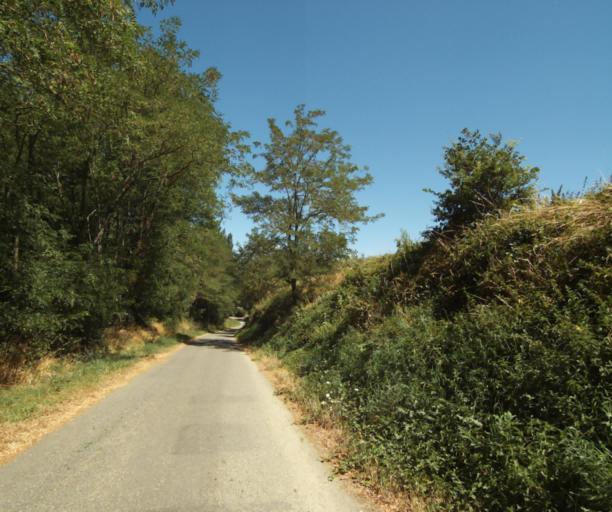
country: FR
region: Midi-Pyrenees
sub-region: Departement de la Haute-Garonne
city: Castanet-Tolosan
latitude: 43.5041
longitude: 1.4935
